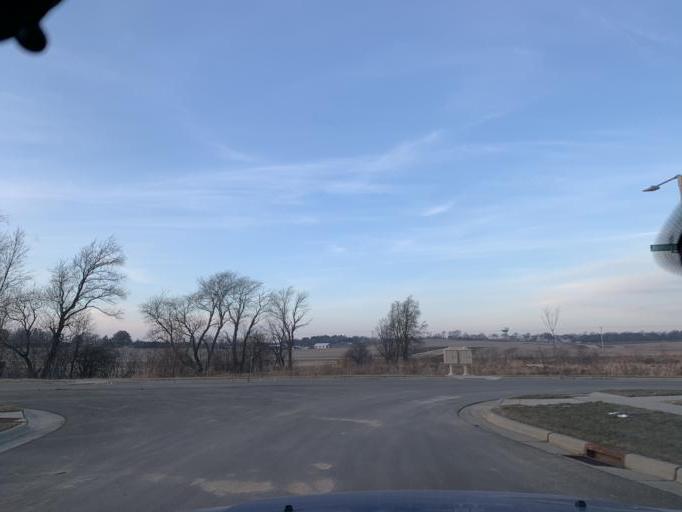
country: US
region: Wisconsin
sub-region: Dane County
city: Middleton
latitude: 43.0586
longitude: -89.5663
